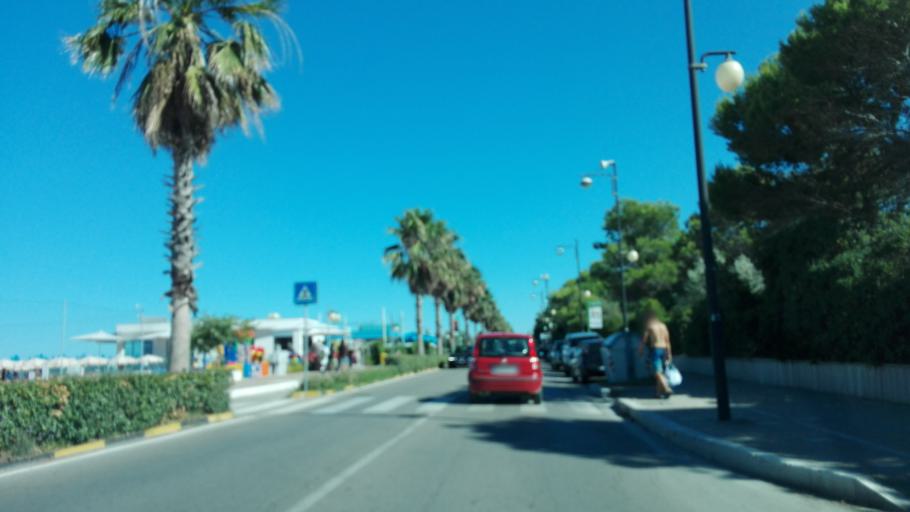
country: IT
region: Abruzzo
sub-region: Provincia di Pescara
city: Montesilvano Marina
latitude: 42.5069
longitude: 14.1719
